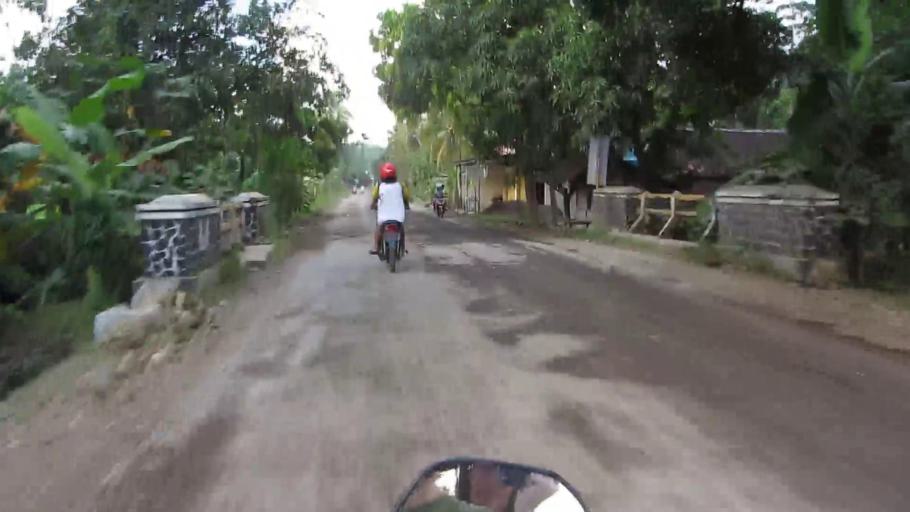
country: ID
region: West Java
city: Binangun
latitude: -7.7163
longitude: 108.4767
